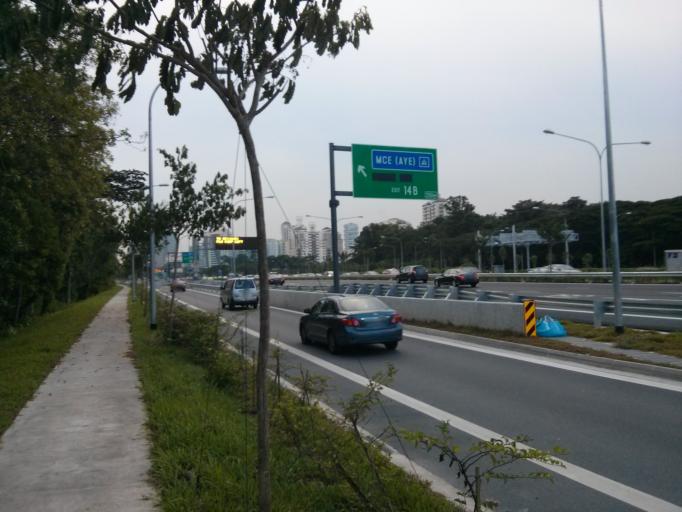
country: SG
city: Singapore
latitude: 1.2953
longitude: 103.8811
